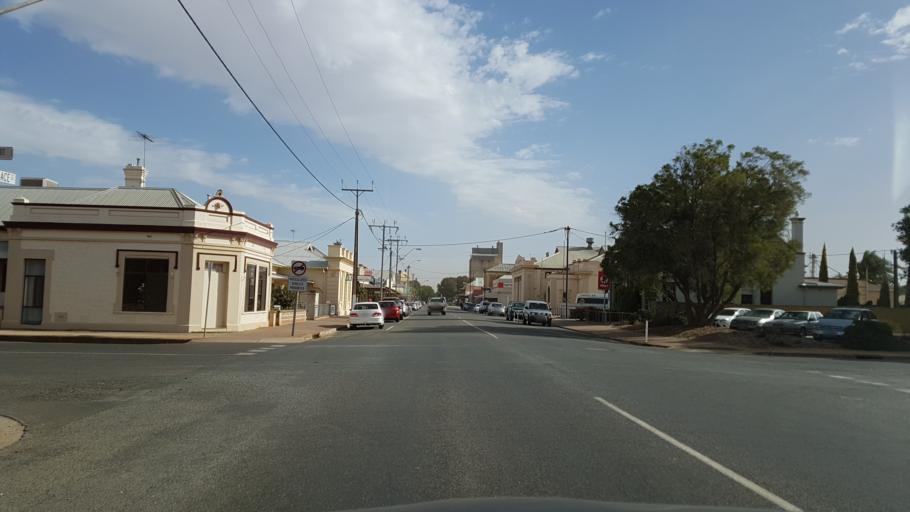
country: AU
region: South Australia
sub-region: Wakefield
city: Balaklava
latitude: -34.1476
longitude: 138.4157
